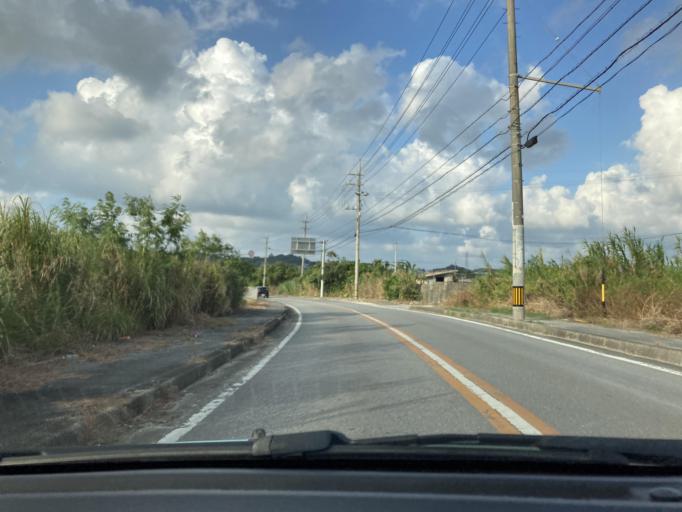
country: JP
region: Okinawa
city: Itoman
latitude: 26.1384
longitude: 127.7003
